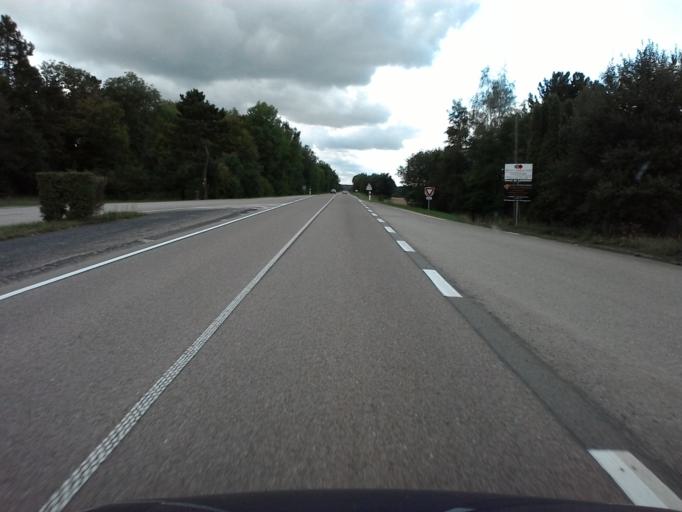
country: FR
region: Lorraine
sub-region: Departement des Vosges
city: Neufchateau
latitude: 48.3857
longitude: 5.7193
